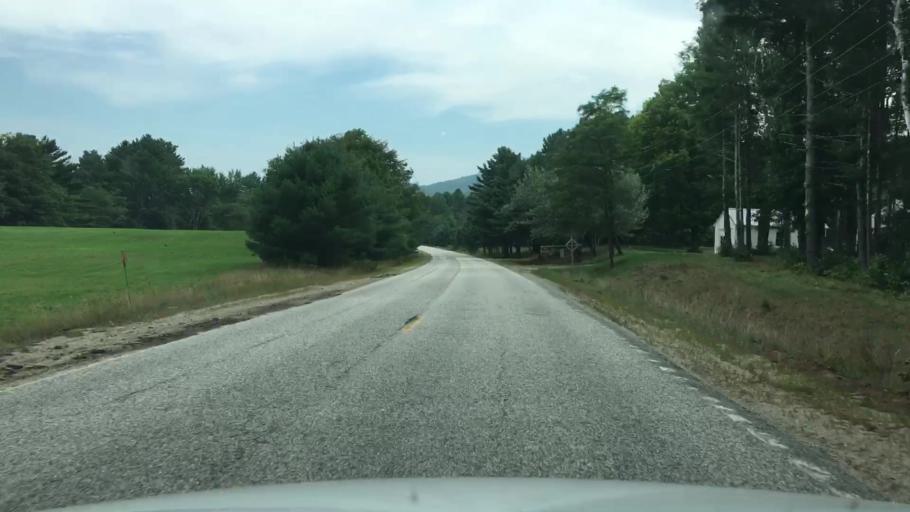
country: US
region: Maine
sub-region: Oxford County
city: Rumford
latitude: 44.5914
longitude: -70.7368
